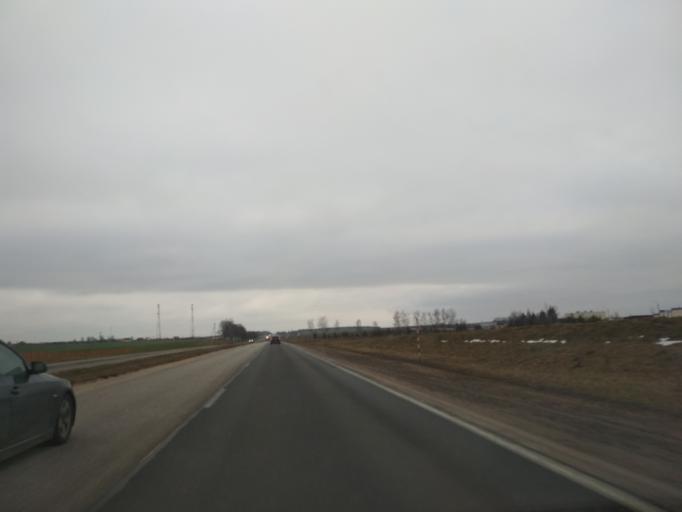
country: BY
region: Minsk
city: Luhavaya Slabada
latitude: 53.7470
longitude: 27.8362
